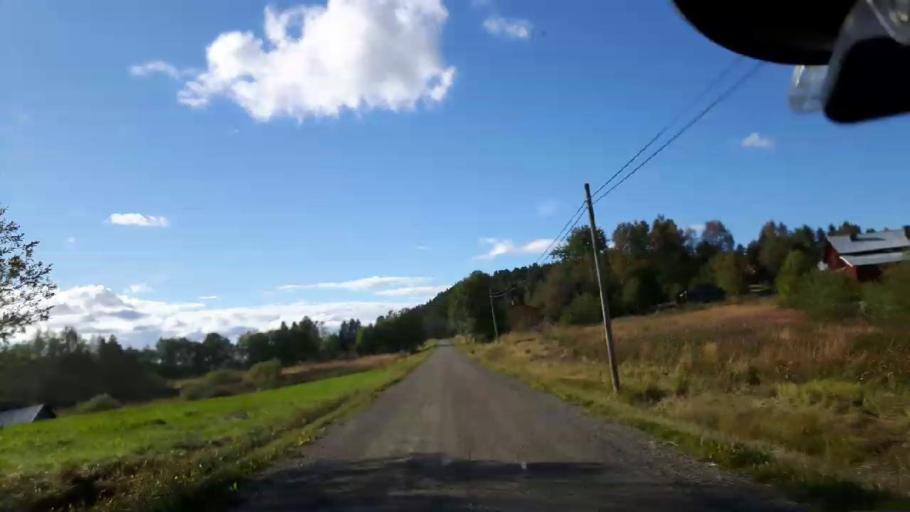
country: SE
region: Jaemtland
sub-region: Ragunda Kommun
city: Hammarstrand
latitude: 63.4738
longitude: 16.1719
